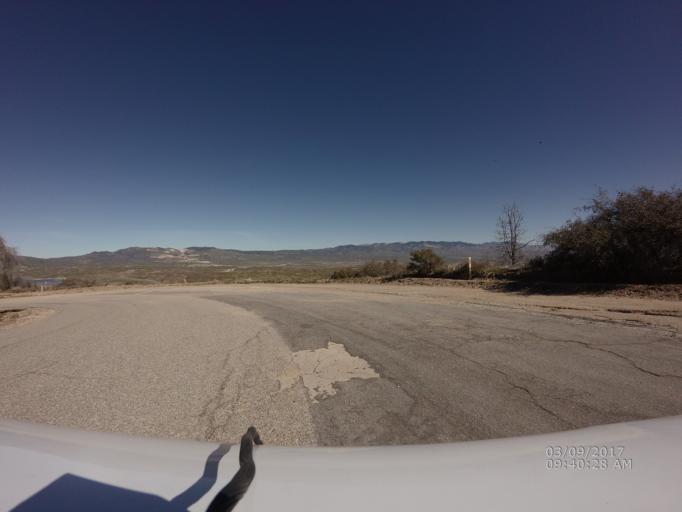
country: US
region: California
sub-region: Kern County
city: Lebec
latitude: 34.7551
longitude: -118.7144
